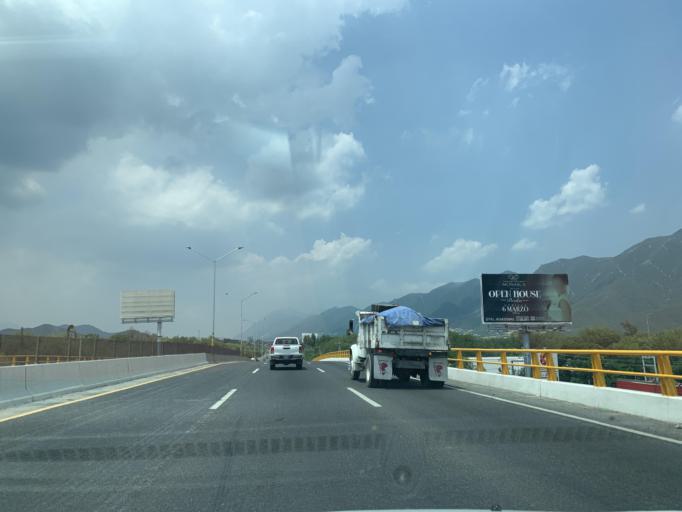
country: MX
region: Nuevo Leon
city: Santiago
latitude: 25.4789
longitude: -100.1793
